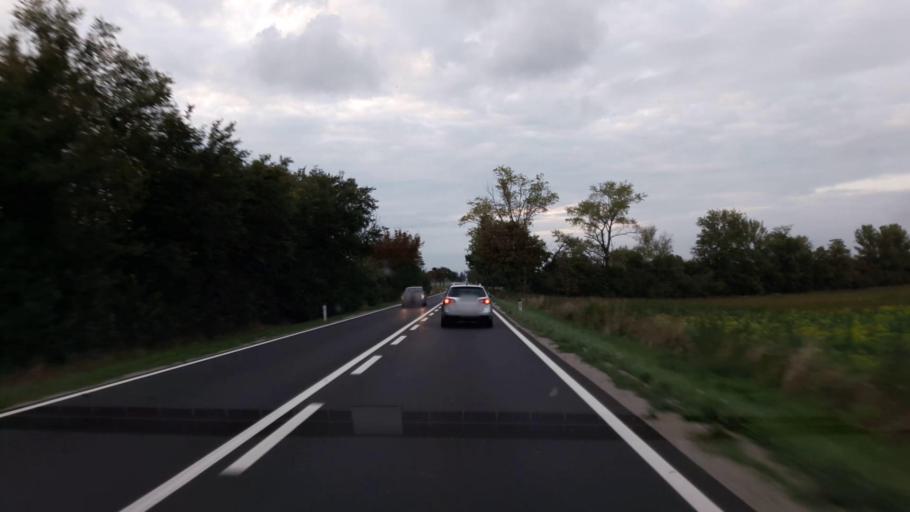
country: AT
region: Lower Austria
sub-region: Politischer Bezirk Wien-Umgebung
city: Rauchenwarth
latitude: 48.1157
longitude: 16.5182
